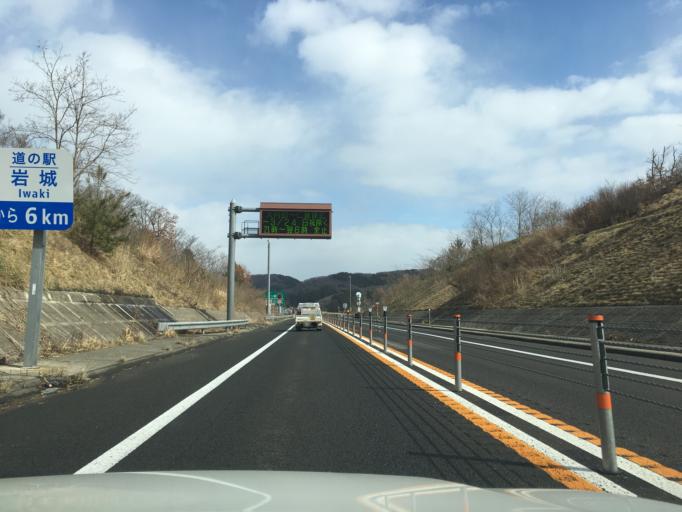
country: JP
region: Akita
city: Akita Shi
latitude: 39.4928
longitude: 140.0577
